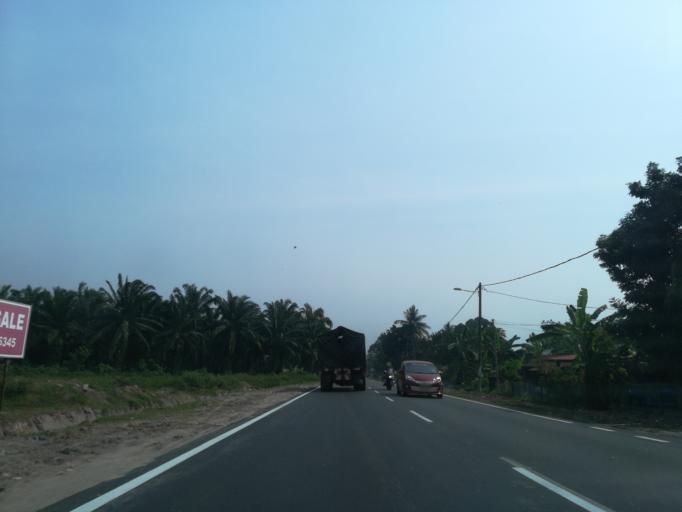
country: MY
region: Penang
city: Tasek Glugor
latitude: 5.4592
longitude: 100.5469
